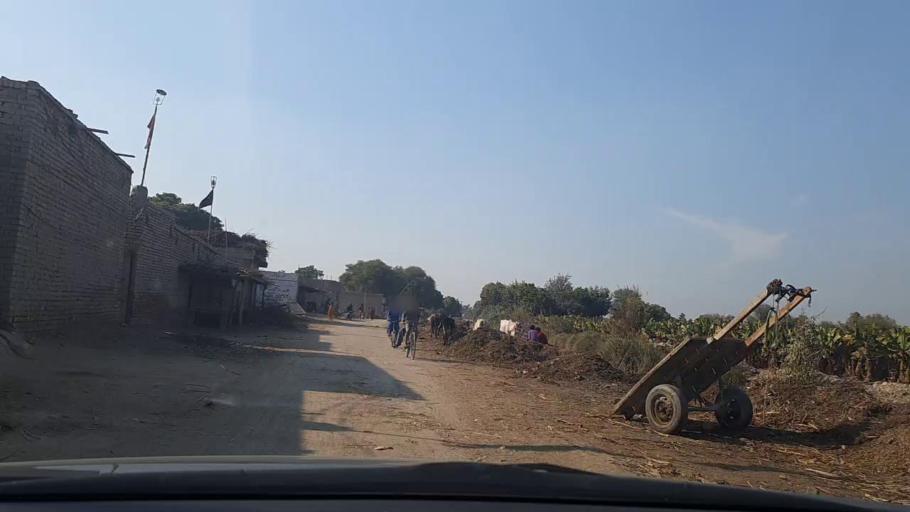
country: PK
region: Sindh
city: Daulatpur
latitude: 26.3050
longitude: 68.0888
